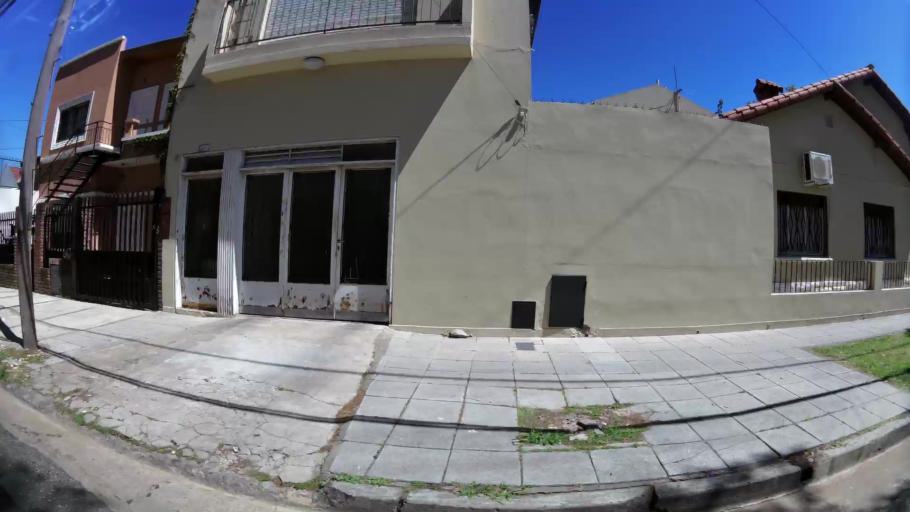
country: AR
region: Buenos Aires
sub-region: Partido de General San Martin
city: General San Martin
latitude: -34.5292
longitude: -58.5408
